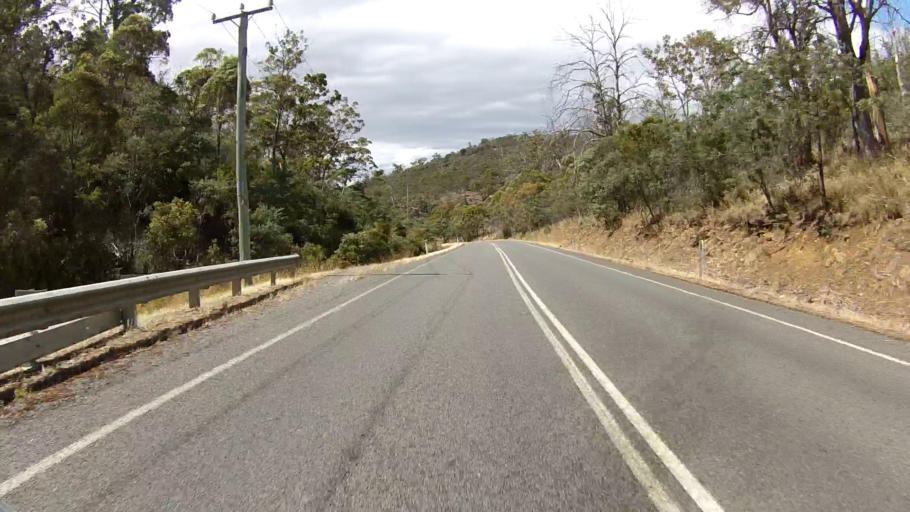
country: AU
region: Tasmania
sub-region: Sorell
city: Sorell
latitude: -42.6067
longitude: 147.6734
